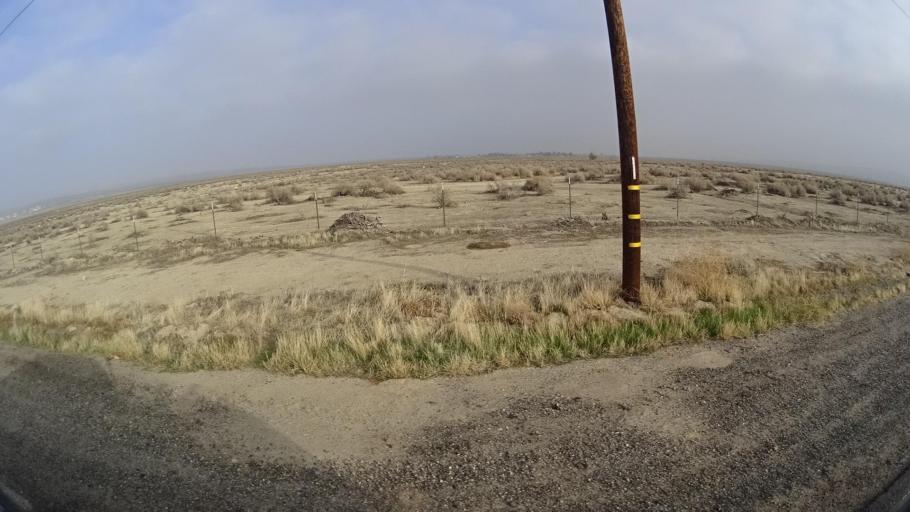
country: US
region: California
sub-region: Kern County
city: Ford City
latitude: 35.2139
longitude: -119.4456
